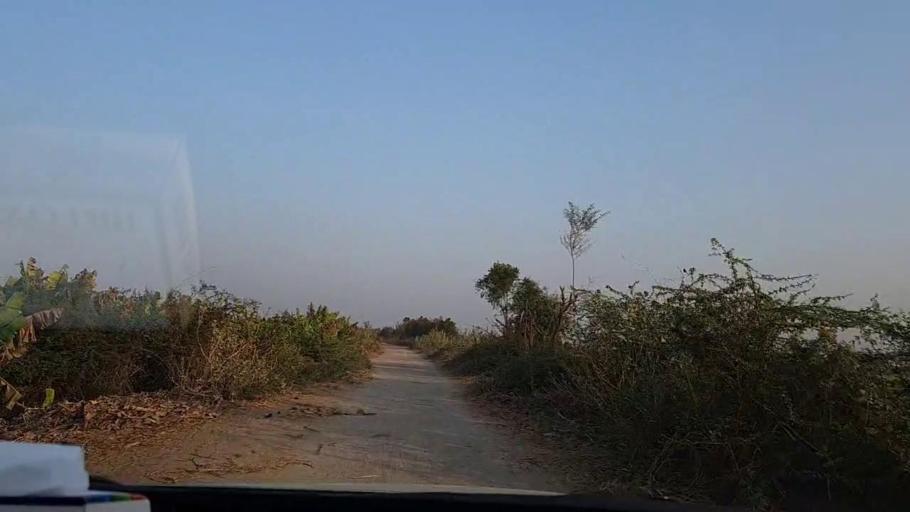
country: PK
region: Sindh
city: Tando Ghulam Ali
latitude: 25.1842
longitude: 68.9140
